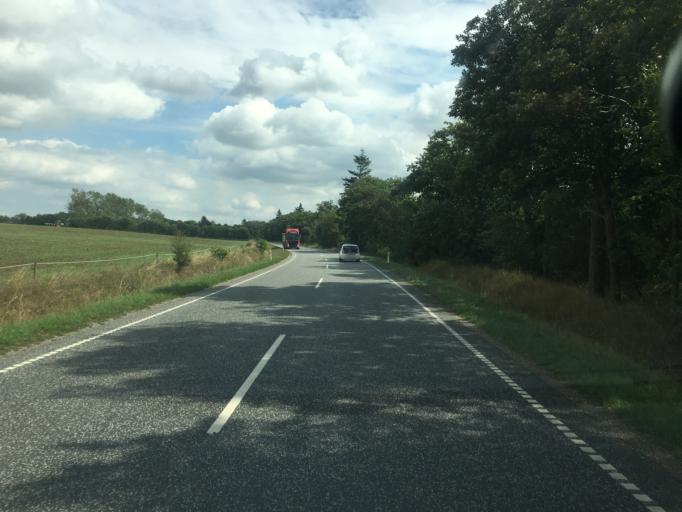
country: DK
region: South Denmark
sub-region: Aabenraa Kommune
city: Aabenraa
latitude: 54.9811
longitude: 9.3640
